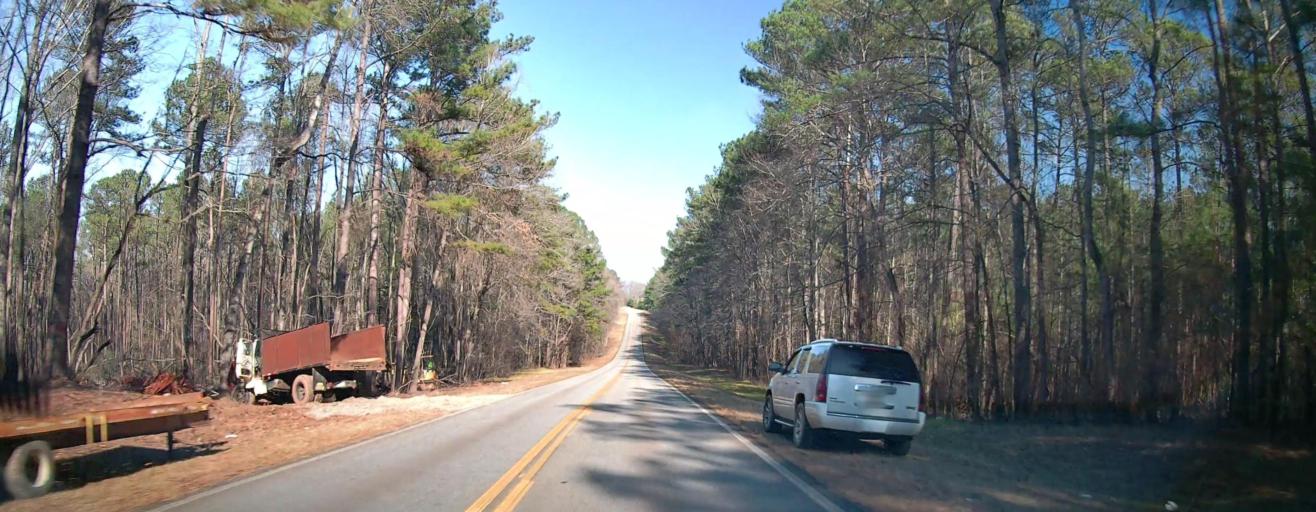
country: US
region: Georgia
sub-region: Monroe County
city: Forsyth
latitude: 33.0815
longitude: -83.8482
